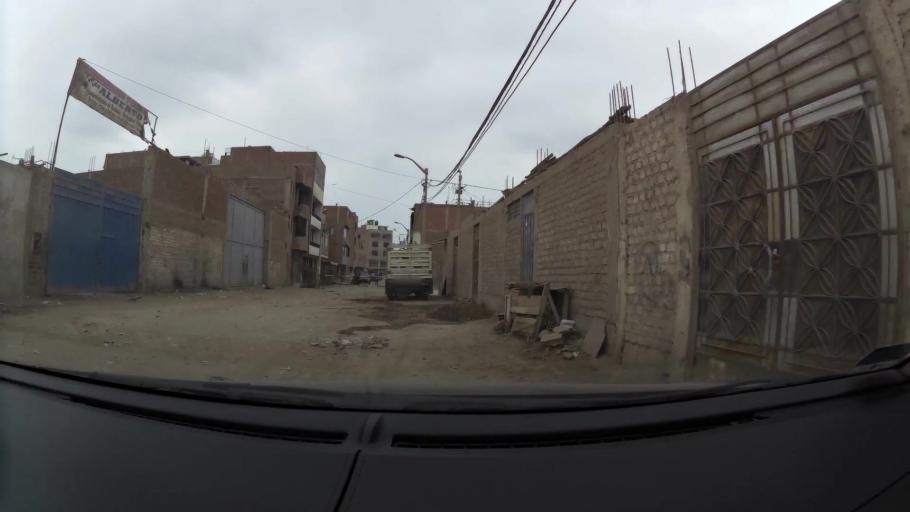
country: PE
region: Lima
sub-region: Lima
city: Independencia
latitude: -11.9722
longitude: -77.0896
